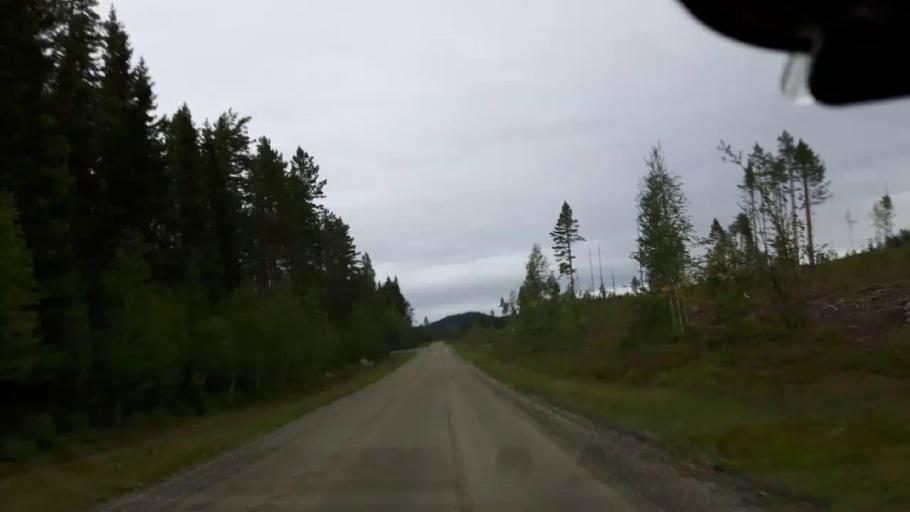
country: SE
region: Vaesternorrland
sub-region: Ange Kommun
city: Fransta
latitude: 62.8629
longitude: 16.0445
